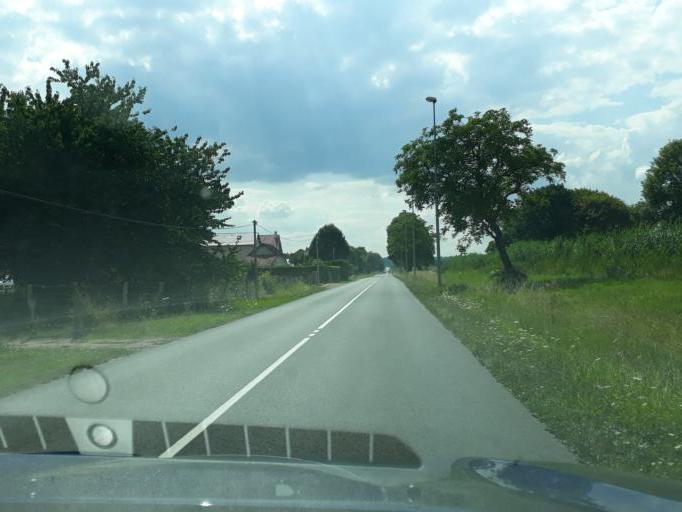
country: FR
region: Bourgogne
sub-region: Departement de la Nievre
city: Fourchambault
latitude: 47.0128
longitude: 3.0594
